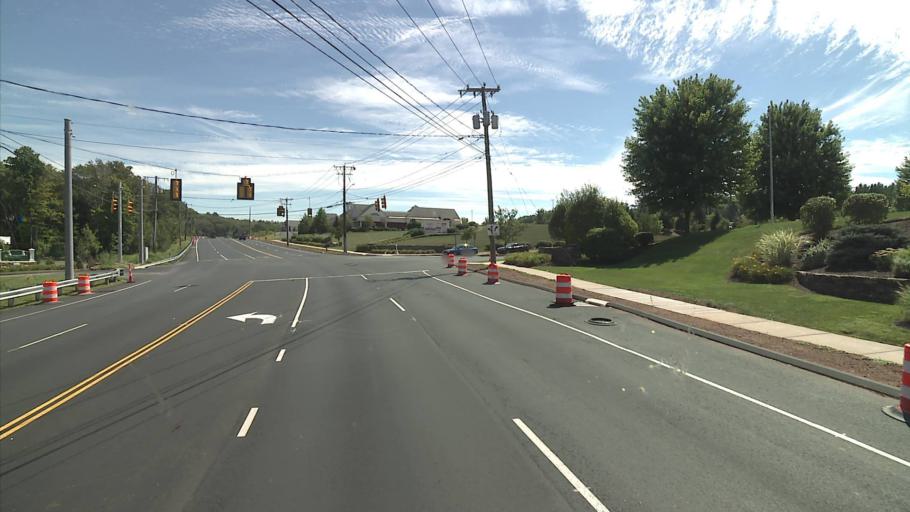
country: US
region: Connecticut
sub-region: Tolland County
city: Tolland
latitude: 41.8616
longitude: -72.3585
